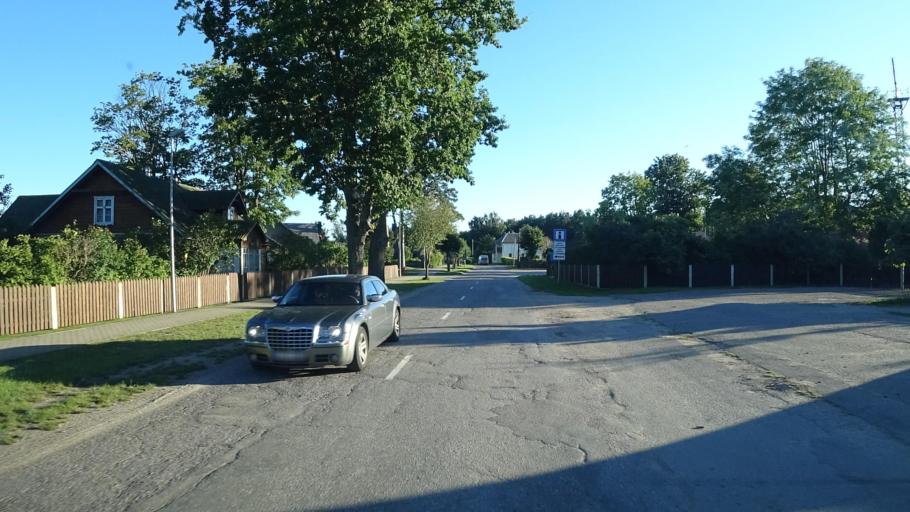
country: LV
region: Dundaga
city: Dundaga
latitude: 57.7429
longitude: 22.5851
